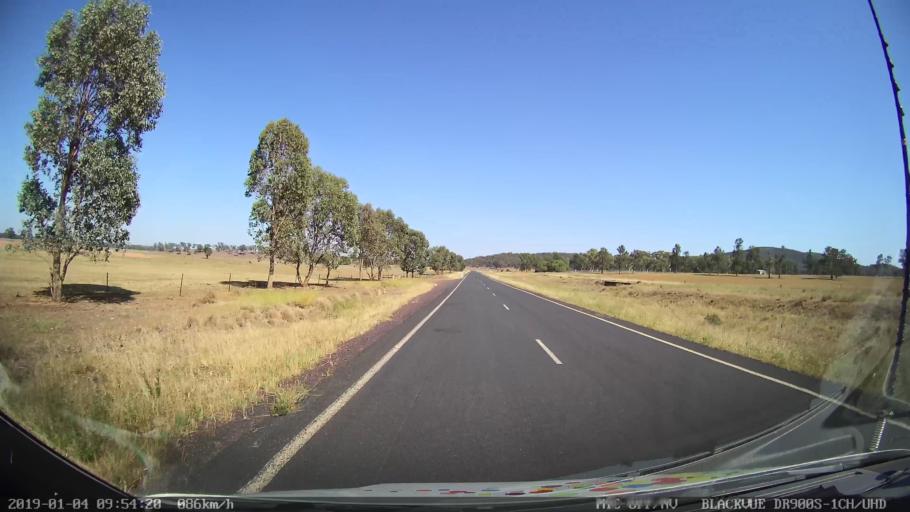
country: AU
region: New South Wales
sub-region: Cabonne
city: Canowindra
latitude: -33.5423
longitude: 148.4160
